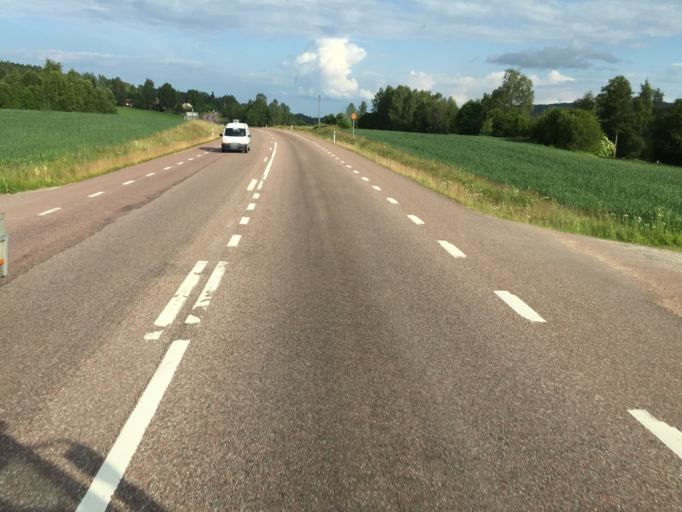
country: SE
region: Dalarna
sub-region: Gagnefs Kommun
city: Djuras
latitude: 60.5372
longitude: 15.2884
